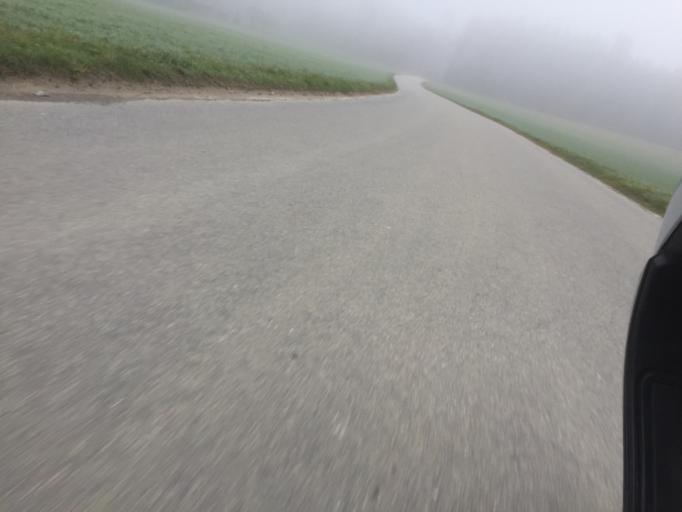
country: CH
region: Bern
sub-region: Seeland District
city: Grossaffoltern
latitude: 47.0976
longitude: 7.3646
